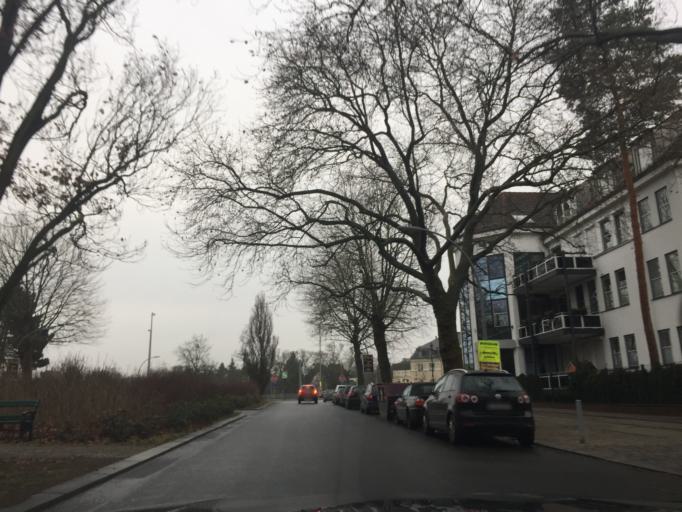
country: DE
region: Berlin
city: Westend
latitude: 52.5097
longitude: 13.2590
